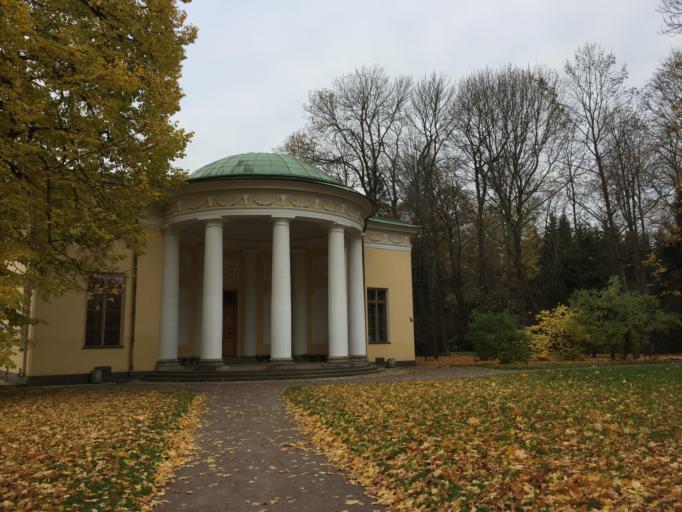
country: RU
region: St.-Petersburg
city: Pushkin
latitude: 59.7129
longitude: 30.3893
